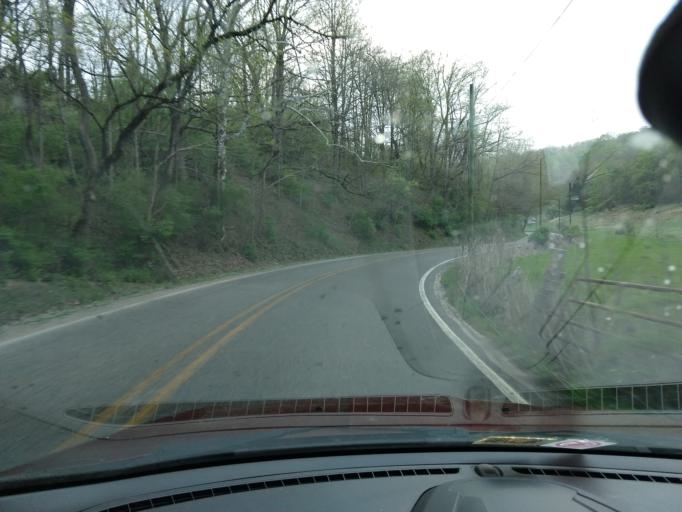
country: US
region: West Virginia
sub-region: Harrison County
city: Despard
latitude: 39.3345
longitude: -80.2825
